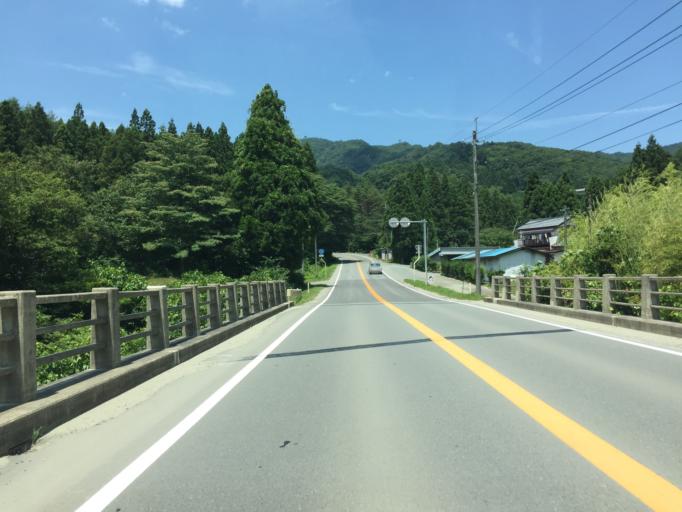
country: JP
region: Miyagi
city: Marumori
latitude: 37.7805
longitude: 140.8242
